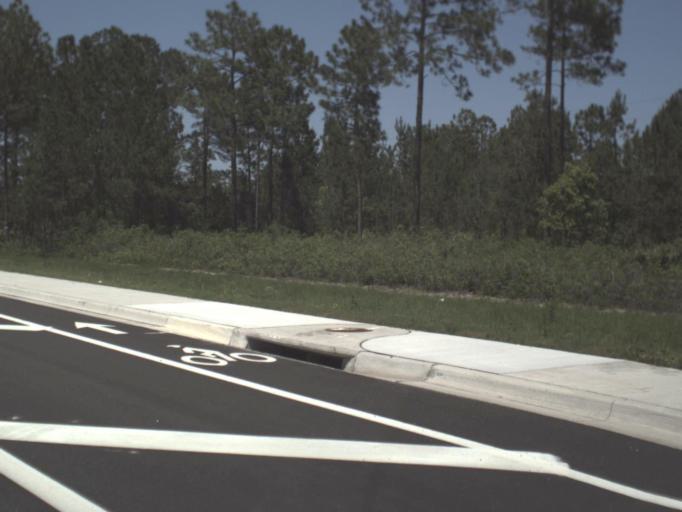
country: US
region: Florida
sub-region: Clay County
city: Lakeside
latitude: 30.1584
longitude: -81.8306
